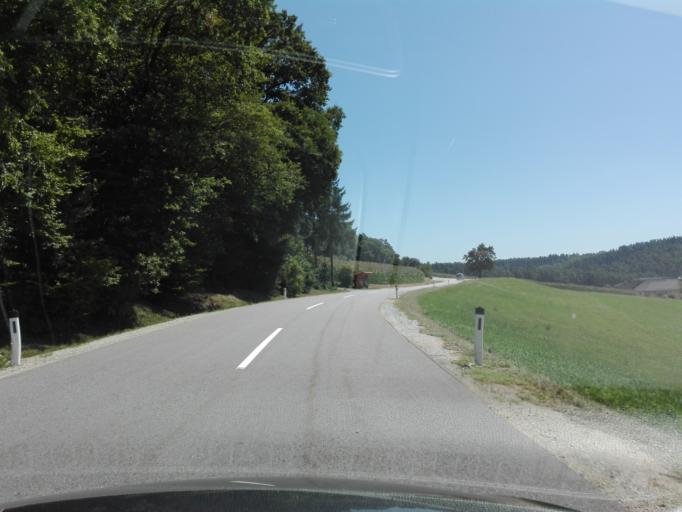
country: AT
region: Upper Austria
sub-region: Politischer Bezirk Urfahr-Umgebung
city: Gallneukirchen
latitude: 48.3330
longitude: 14.4015
